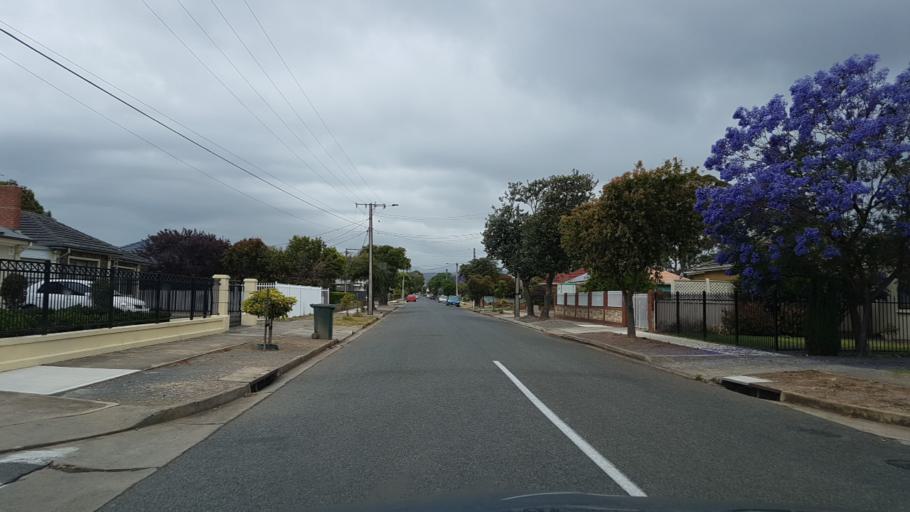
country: AU
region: South Australia
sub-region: Marion
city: South Plympton
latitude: -34.9766
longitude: 138.5512
